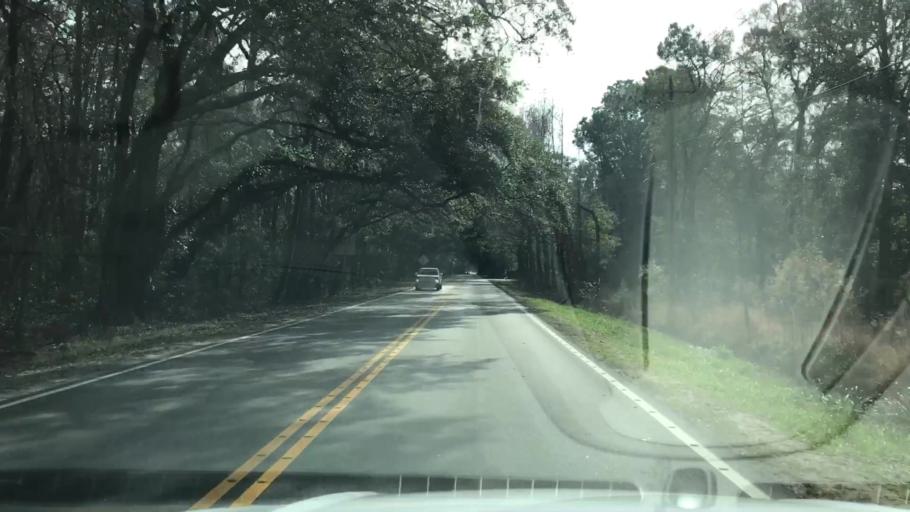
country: US
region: South Carolina
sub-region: Charleston County
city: Shell Point
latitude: 32.7410
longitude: -80.0363
